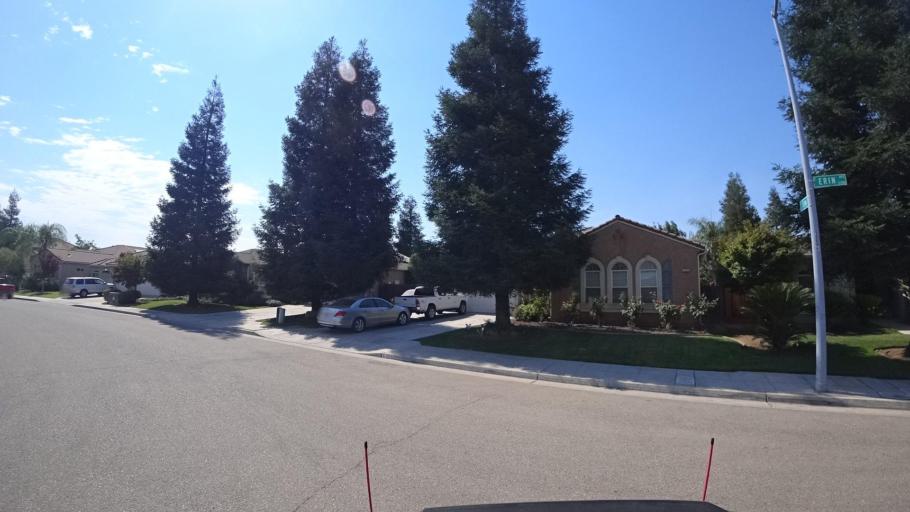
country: US
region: California
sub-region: Fresno County
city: Sunnyside
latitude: 36.7214
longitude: -119.6928
